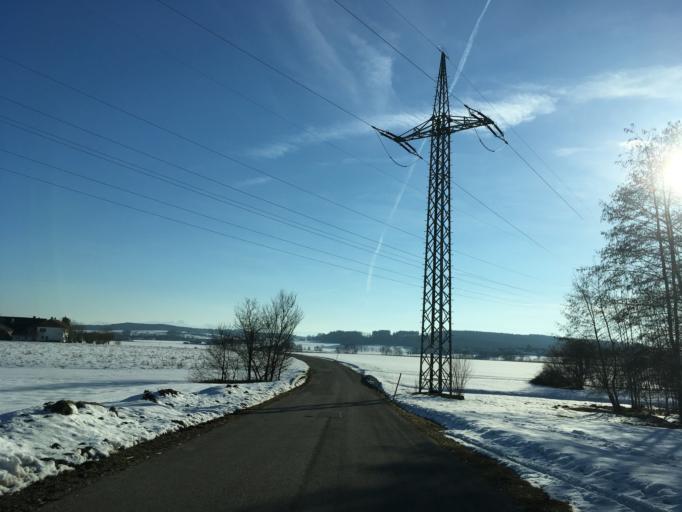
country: DE
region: Bavaria
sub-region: Upper Bavaria
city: Steinhoring
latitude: 48.1069
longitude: 12.0263
